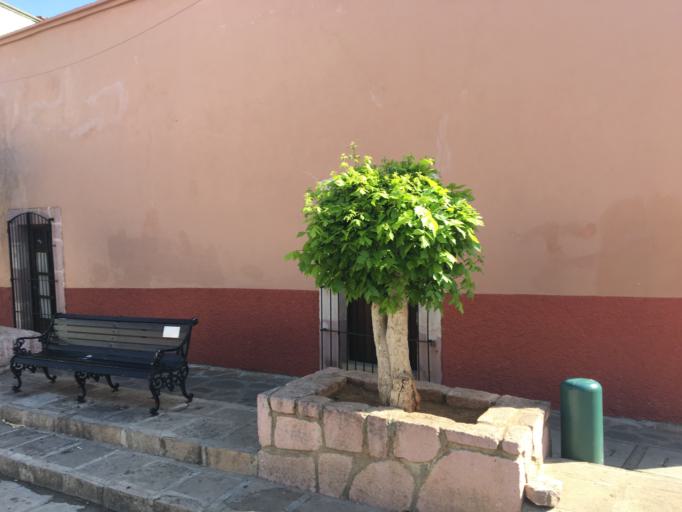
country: MX
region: Zacatecas
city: Zacatecas
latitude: 22.7823
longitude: -102.5713
